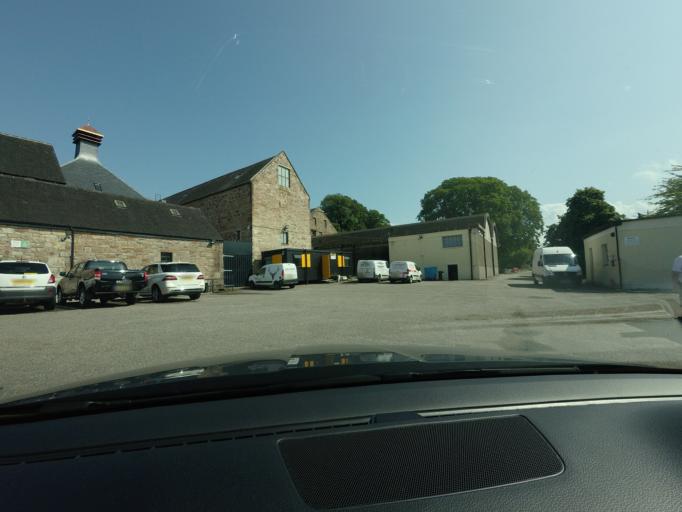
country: GB
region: Scotland
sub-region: Highland
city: Alness
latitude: 57.6882
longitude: -4.2390
